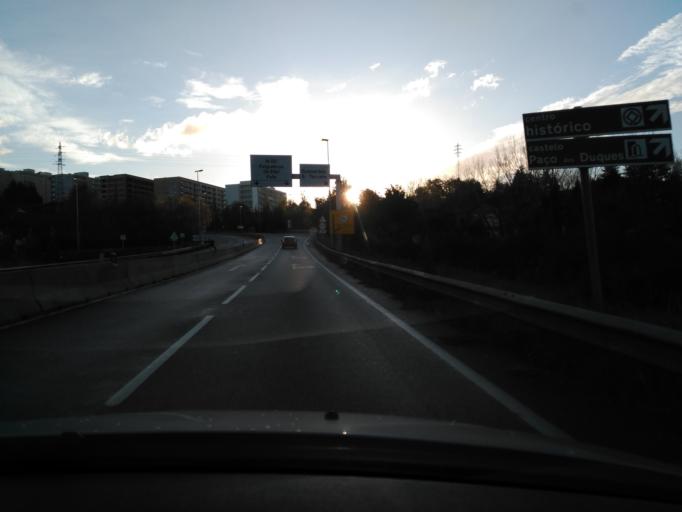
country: PT
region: Braga
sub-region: Guimaraes
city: Guimaraes
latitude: 41.4549
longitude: -8.2861
